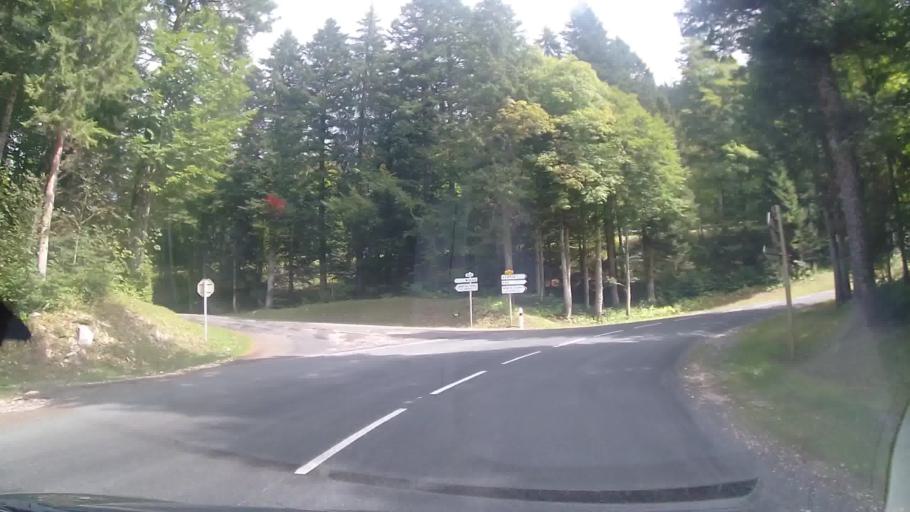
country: FR
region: Rhone-Alpes
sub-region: Departement de l'Ain
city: Gex
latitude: 46.3829
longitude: 6.0459
